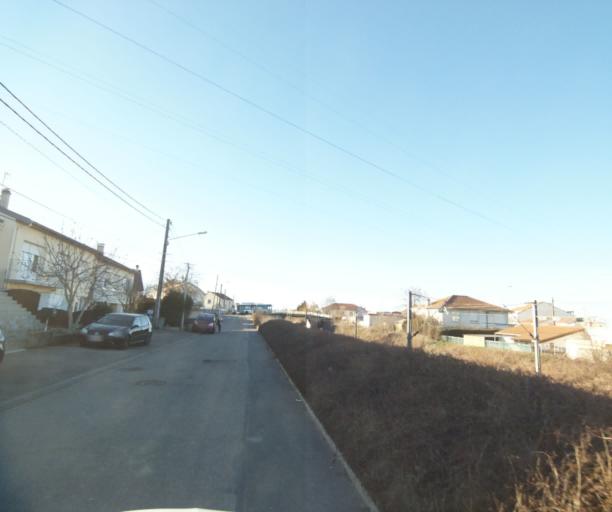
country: FR
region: Lorraine
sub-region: Departement de Meurthe-et-Moselle
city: Laneuveville-devant-Nancy
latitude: 48.6510
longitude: 6.2348
